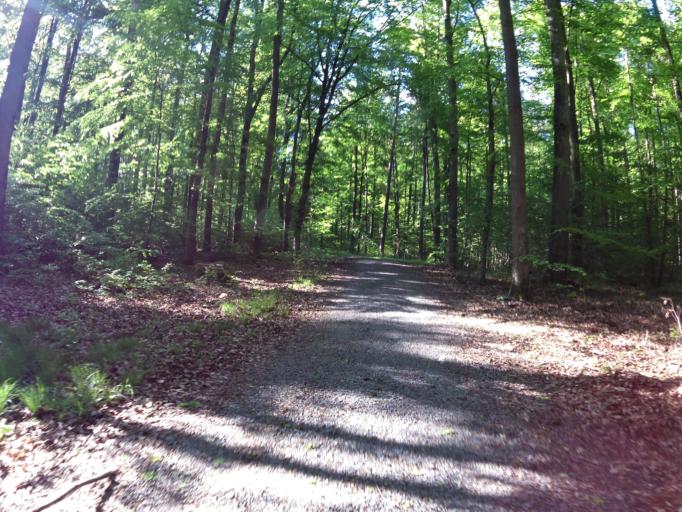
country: DE
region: Bavaria
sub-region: Regierungsbezirk Unterfranken
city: Reichenberg
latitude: 49.7465
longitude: 9.9041
